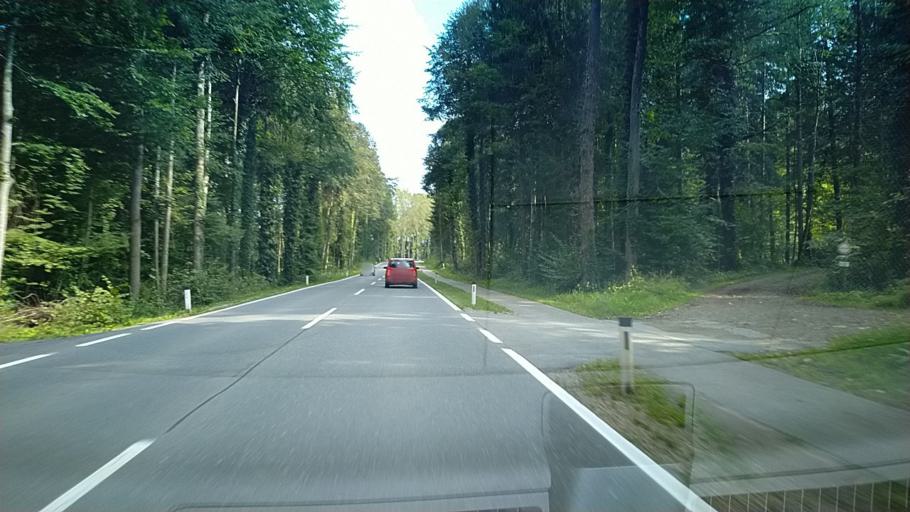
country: AT
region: Styria
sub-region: Politischer Bezirk Deutschlandsberg
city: Hollenegg
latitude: 46.7889
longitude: 15.2271
